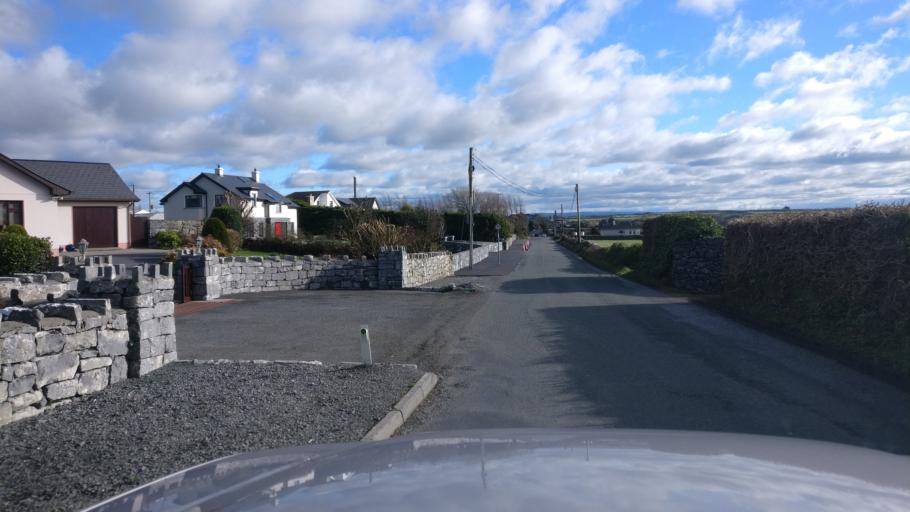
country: IE
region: Connaught
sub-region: County Galway
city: Oranmore
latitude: 53.2764
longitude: -8.8891
